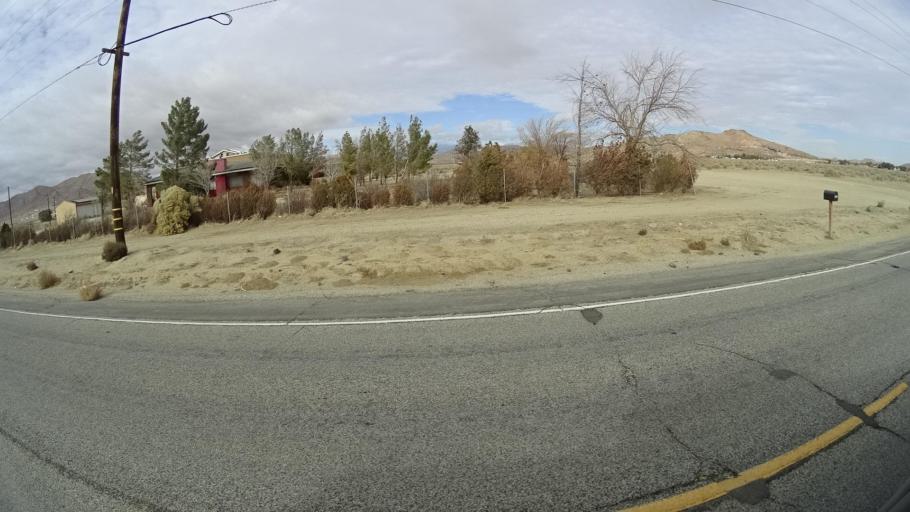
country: US
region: California
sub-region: Kern County
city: Rosamond
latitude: 34.8632
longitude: -118.2465
